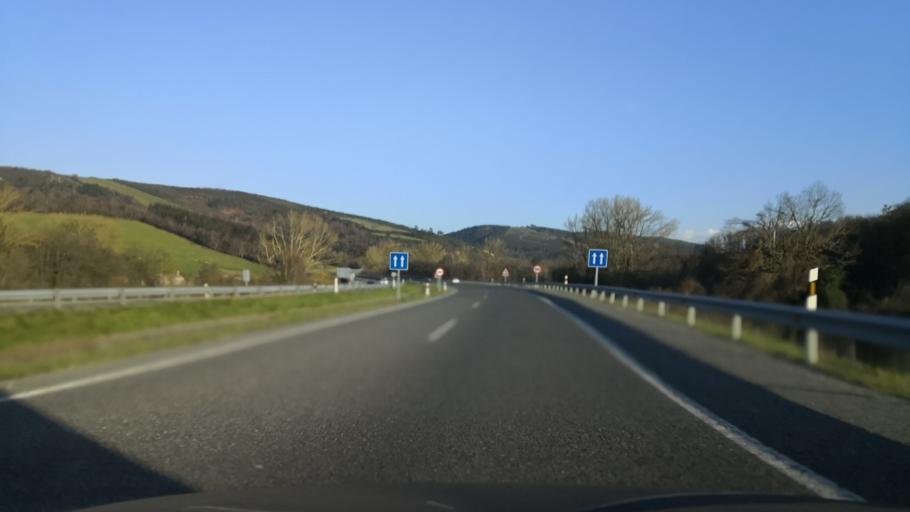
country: ES
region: Galicia
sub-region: Provincia de Lugo
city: Baralla
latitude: 42.9184
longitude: -7.2076
